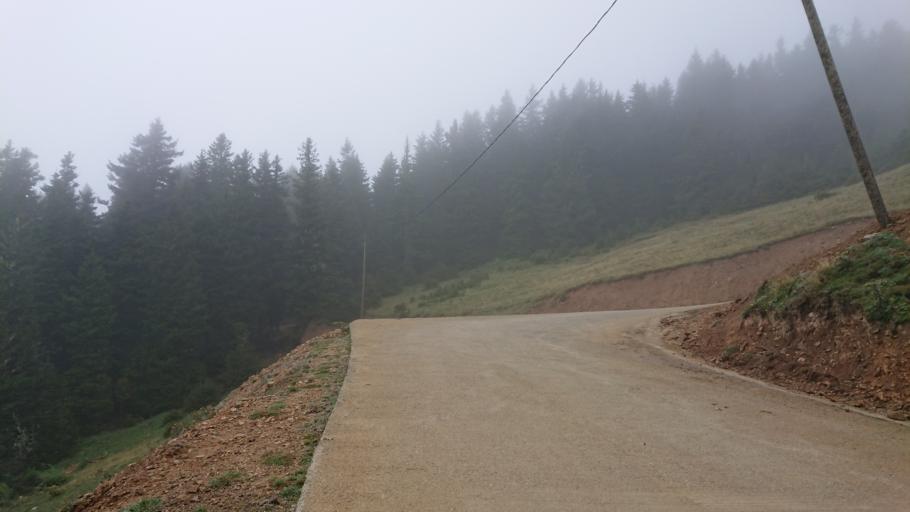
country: TR
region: Gumushane
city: Kurtun
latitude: 40.6716
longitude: 38.9981
